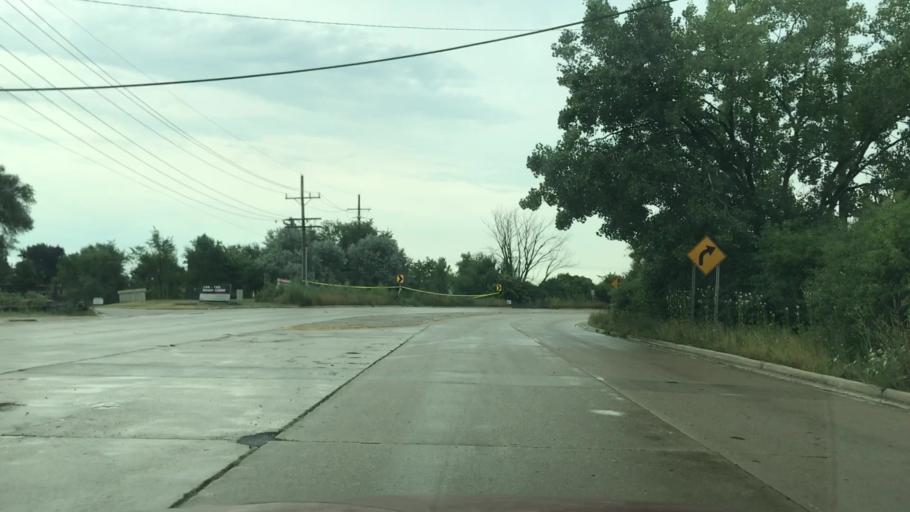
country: US
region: Illinois
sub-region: Cook County
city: Rosemont
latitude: 42.0111
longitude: -87.9207
